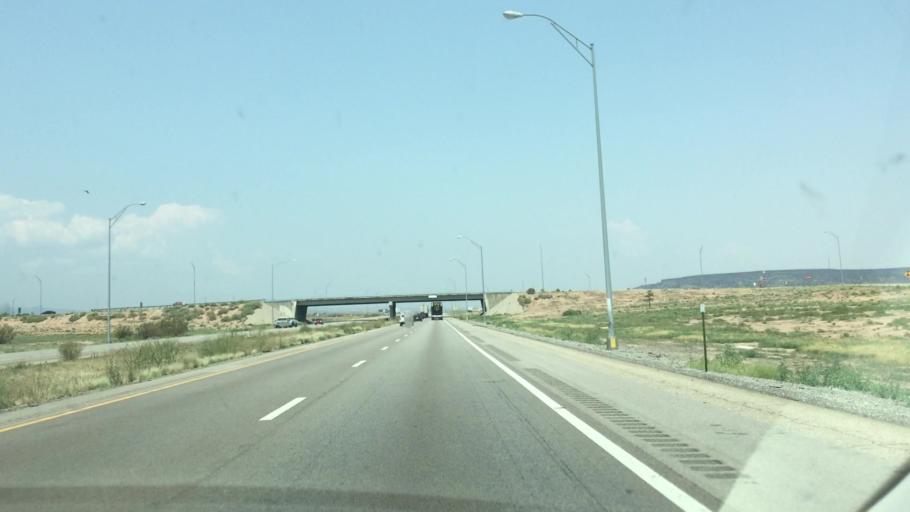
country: US
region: New Mexico
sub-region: Cibola County
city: Grants
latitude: 35.1225
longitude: -107.8271
